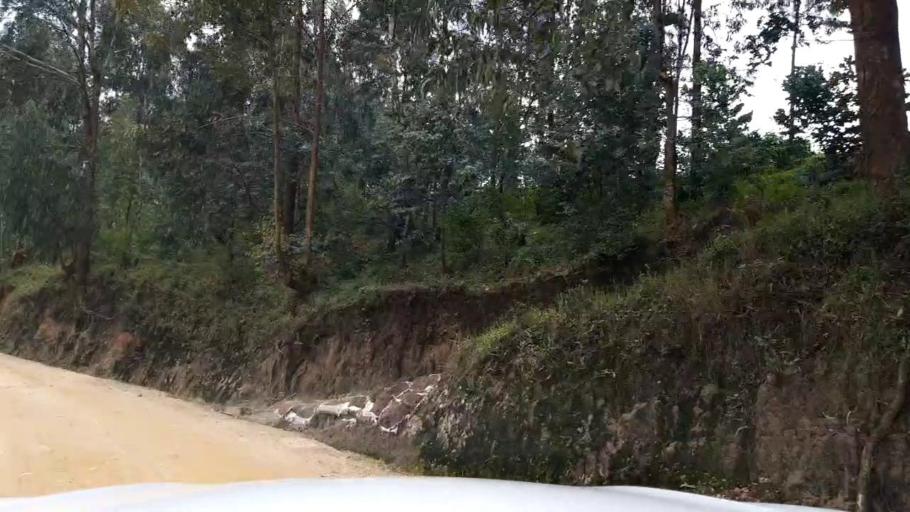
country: RW
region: Western Province
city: Kibuye
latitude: -1.9666
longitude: 29.3904
